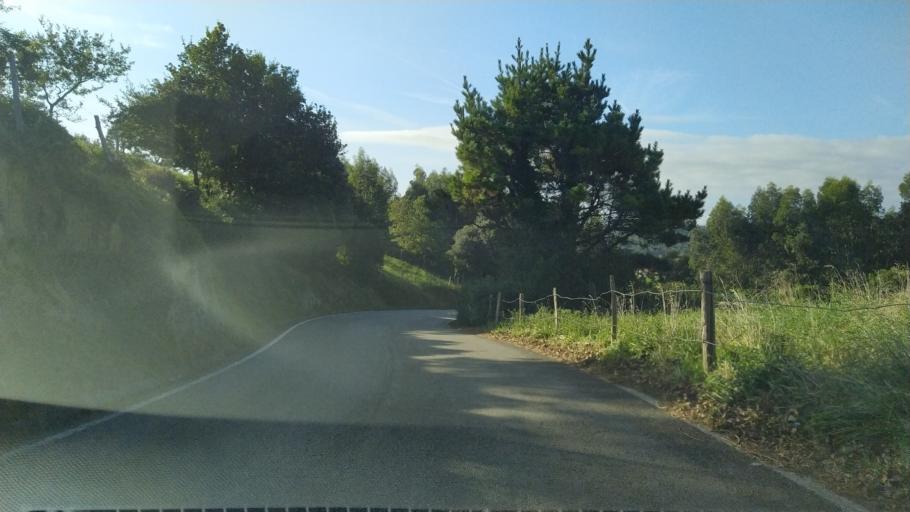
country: ES
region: Cantabria
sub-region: Provincia de Cantabria
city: Santa Cruz de Bezana
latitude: 43.4516
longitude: -3.9283
